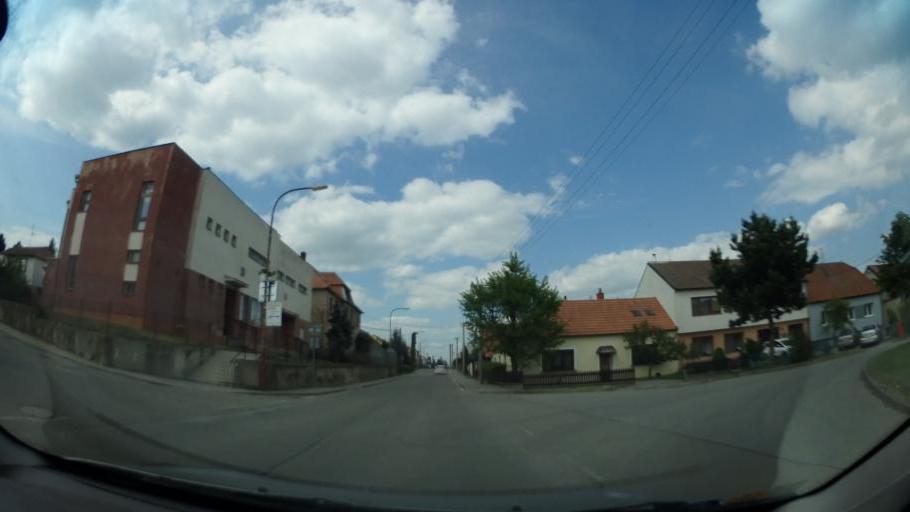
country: CZ
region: Vysocina
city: Mohelno
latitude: 49.1155
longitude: 16.1948
